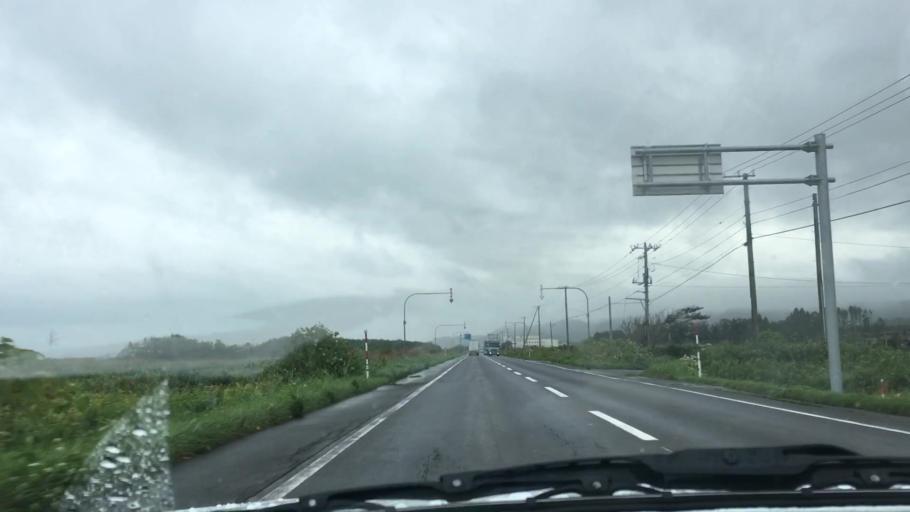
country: JP
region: Hokkaido
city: Niseko Town
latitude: 42.3947
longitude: 140.3002
